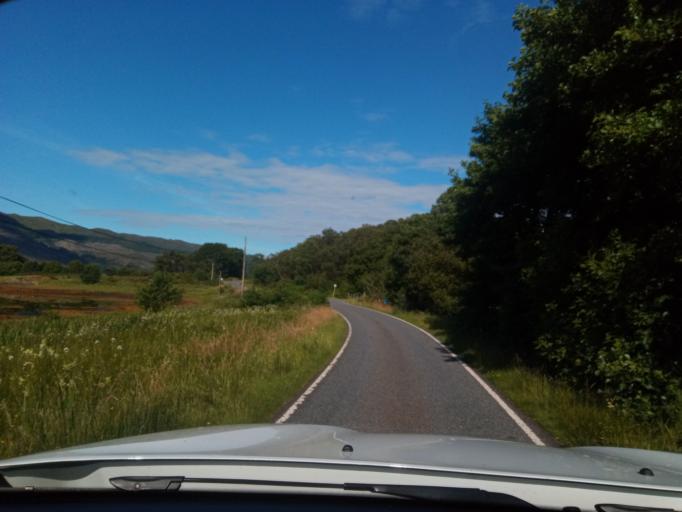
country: GB
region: Scotland
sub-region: Argyll and Bute
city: Isle Of Mull
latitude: 56.6889
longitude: -5.6638
